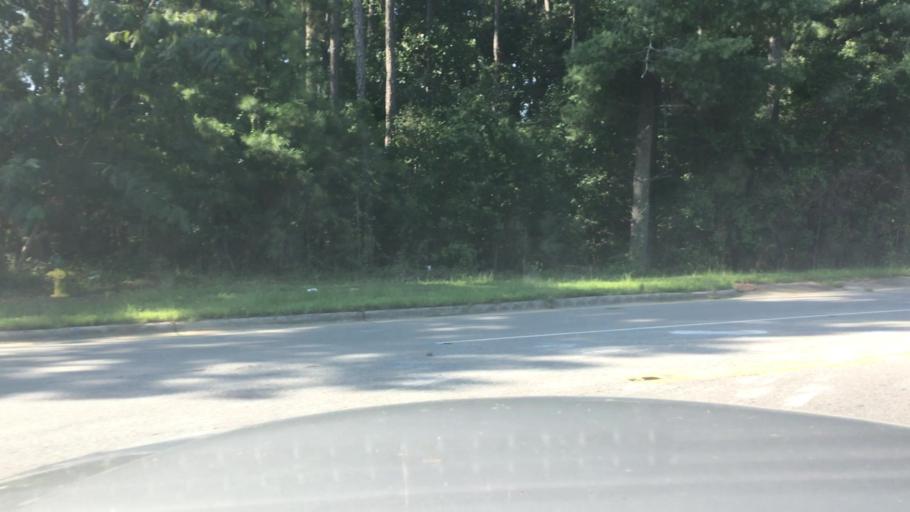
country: US
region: North Carolina
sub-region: Cumberland County
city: Spring Lake
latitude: 35.1544
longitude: -78.9093
